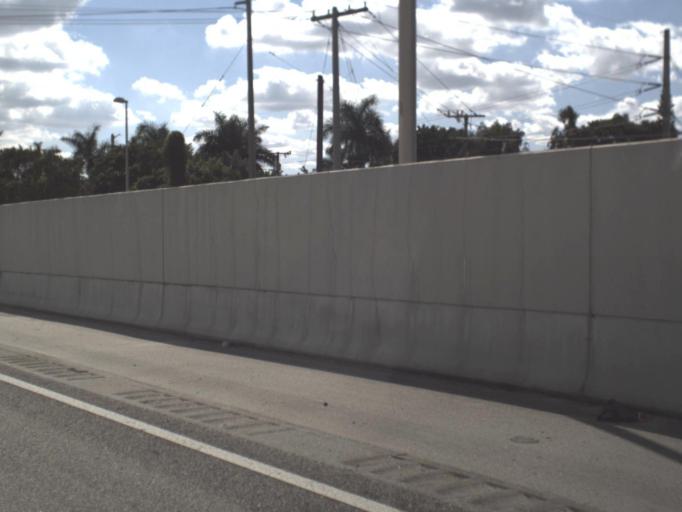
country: US
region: Florida
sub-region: Broward County
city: Davie
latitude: 26.0631
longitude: -80.2155
